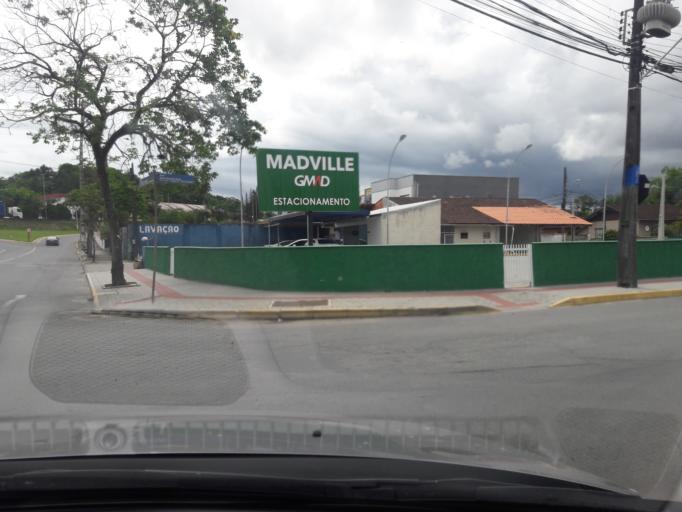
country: BR
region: Santa Catarina
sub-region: Joinville
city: Joinville
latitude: -26.3247
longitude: -48.8651
